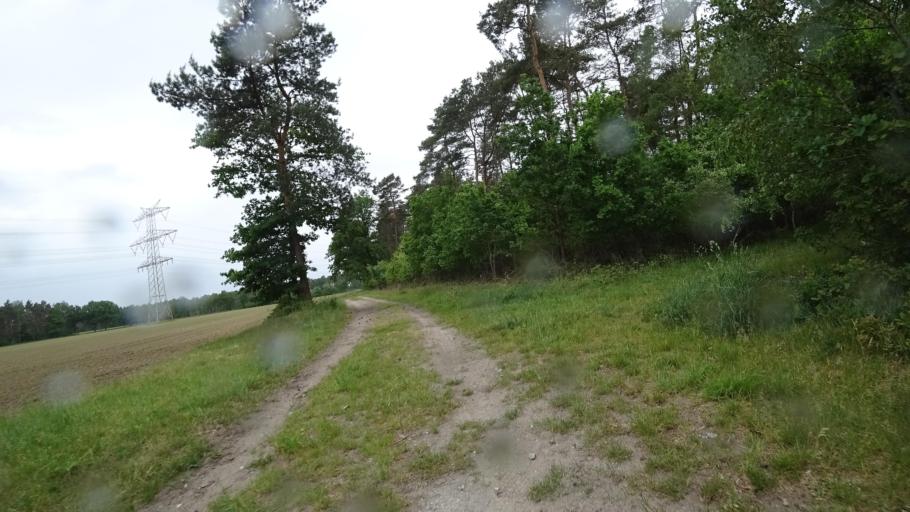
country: DE
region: North Rhine-Westphalia
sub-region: Regierungsbezirk Detmold
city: Rheda-Wiedenbruck
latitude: 51.9075
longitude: 8.2942
